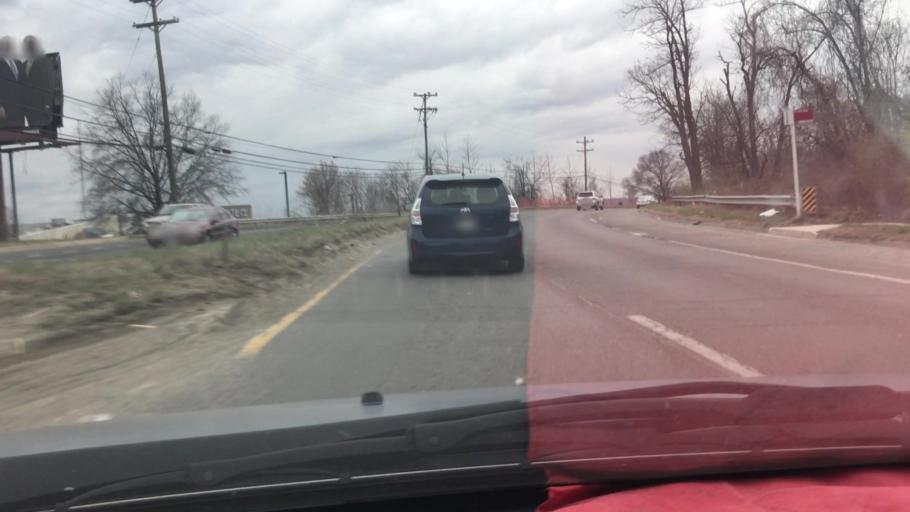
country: US
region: Maryland
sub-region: Prince George's County
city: Cheverly
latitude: 38.9260
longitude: -76.9281
